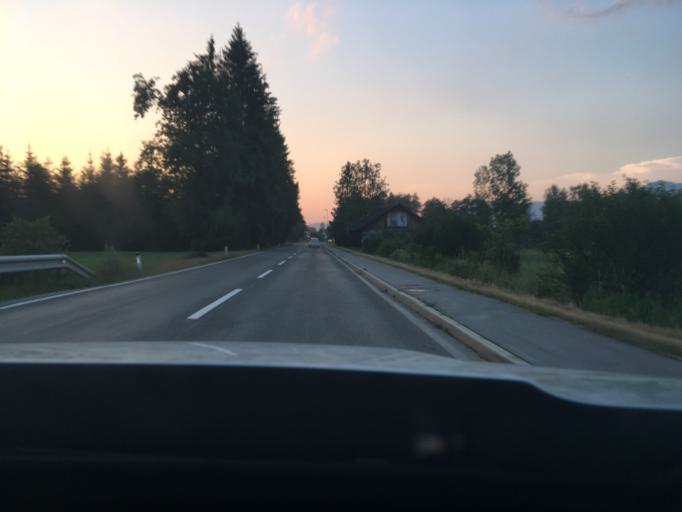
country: SI
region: Ribnica
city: Ribnica
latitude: 45.7261
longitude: 14.7395
